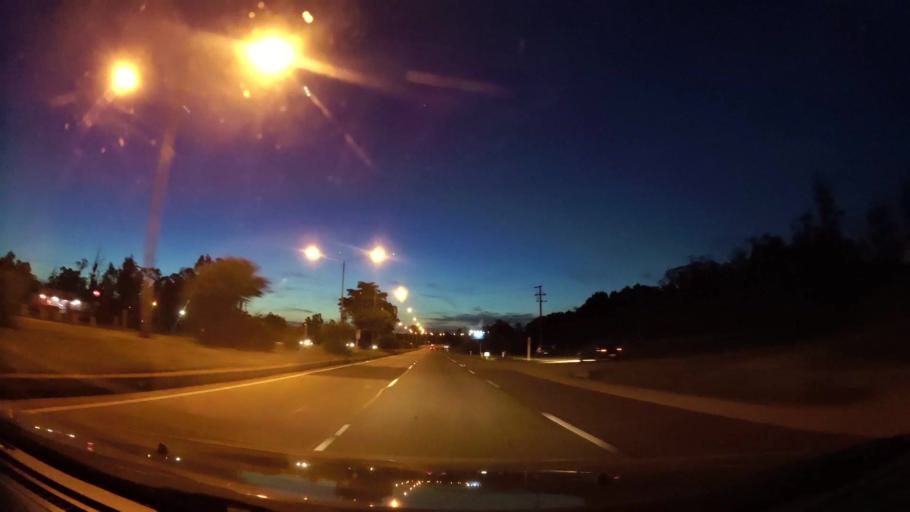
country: UY
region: Canelones
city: Atlantida
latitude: -34.7673
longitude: -55.7691
